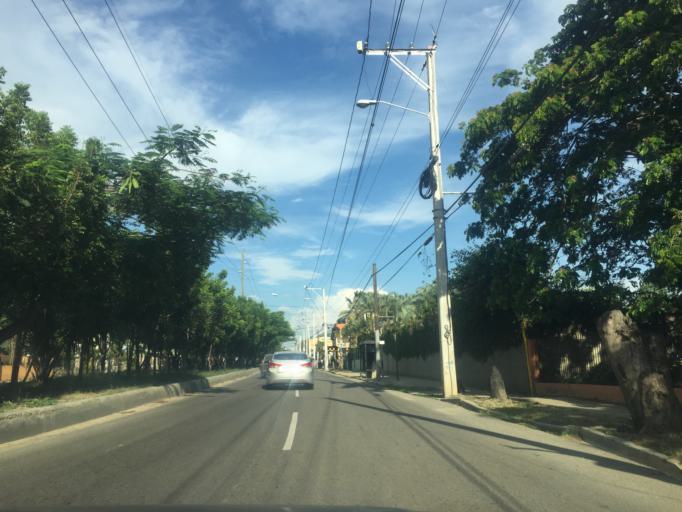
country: DO
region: Santiago
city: Santiago de los Caballeros
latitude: 19.4443
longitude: -70.7400
